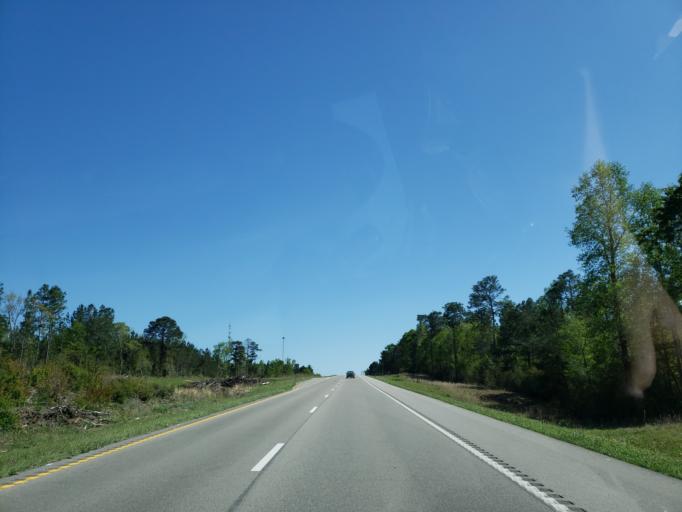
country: US
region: Mississippi
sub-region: Stone County
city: Wiggins
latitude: 30.9615
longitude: -89.1925
